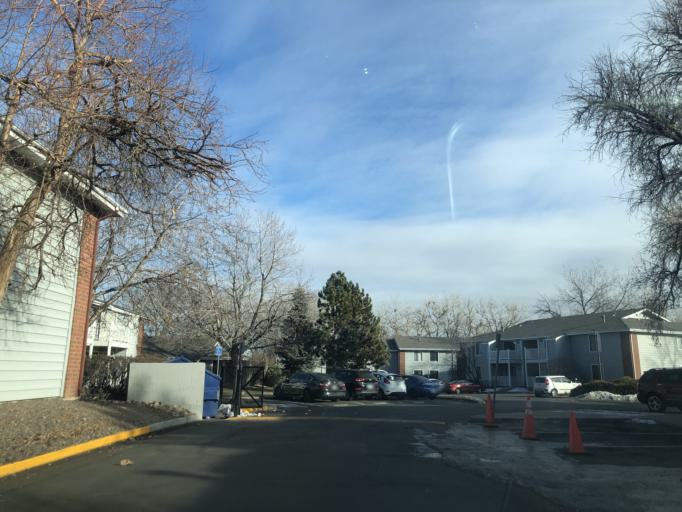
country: US
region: Colorado
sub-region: Adams County
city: Aurora
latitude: 39.7013
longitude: -104.8078
